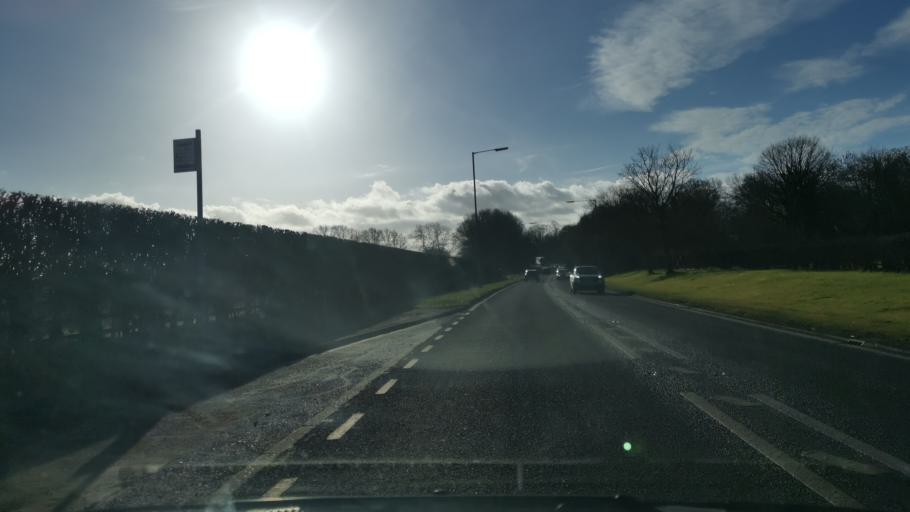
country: GB
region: England
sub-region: City of York
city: Skelton
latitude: 53.9938
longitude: -1.1306
